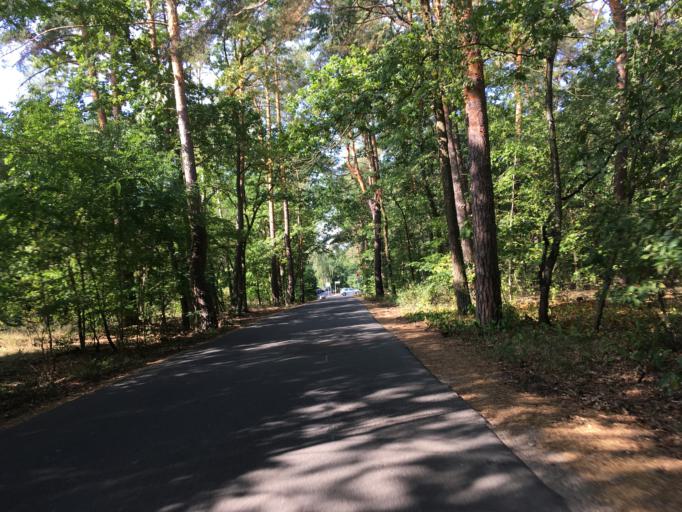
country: DE
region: Berlin
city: Rahnsdorf
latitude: 52.4235
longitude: 13.6822
